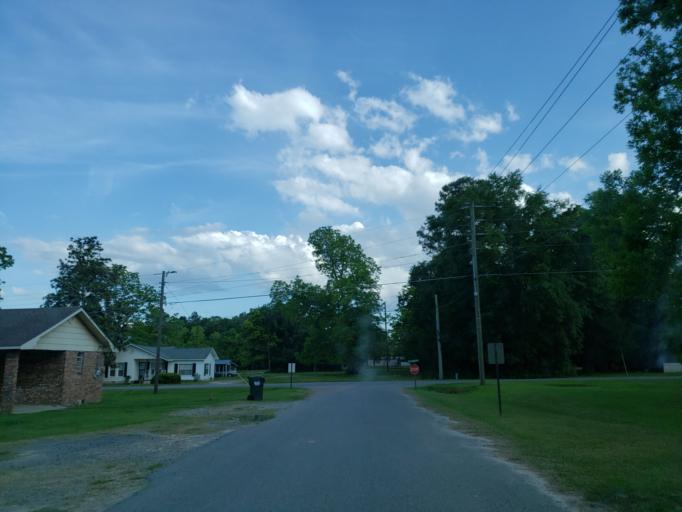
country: US
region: Georgia
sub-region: Lowndes County
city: Hahira
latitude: 31.0461
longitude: -83.3917
